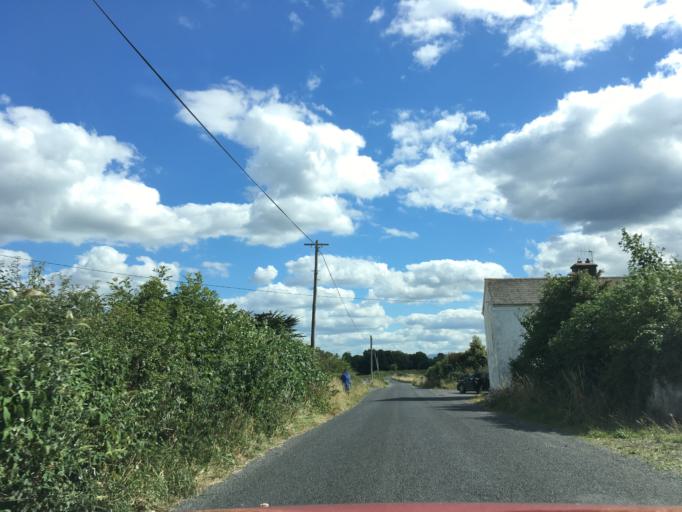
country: IE
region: Munster
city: Cahir
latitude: 52.4614
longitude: -7.9722
